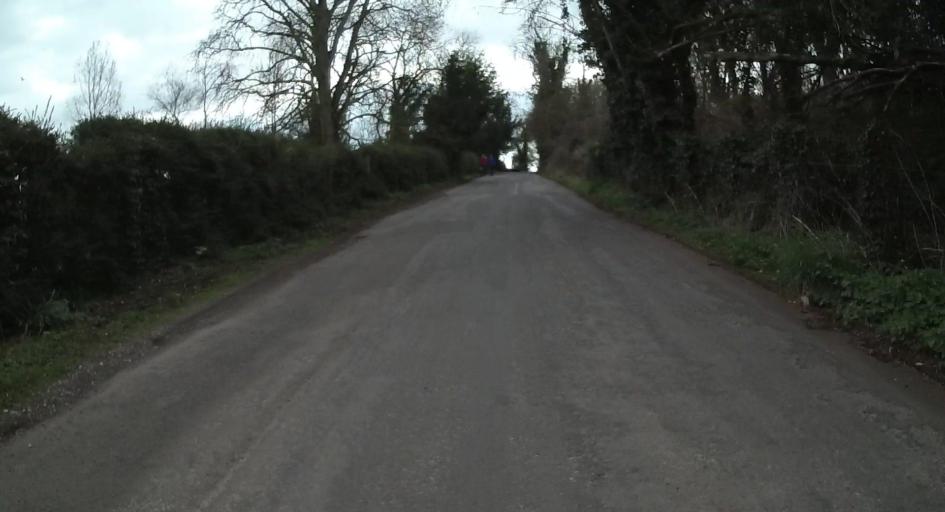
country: GB
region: England
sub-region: Hampshire
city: Andover
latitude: 51.1577
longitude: -1.4558
